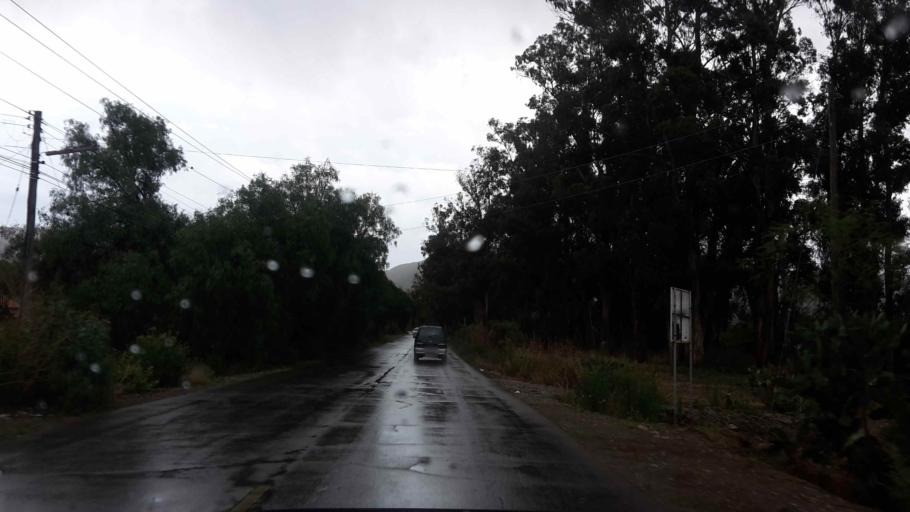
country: BO
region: Cochabamba
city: Tarata
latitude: -17.5434
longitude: -66.1055
